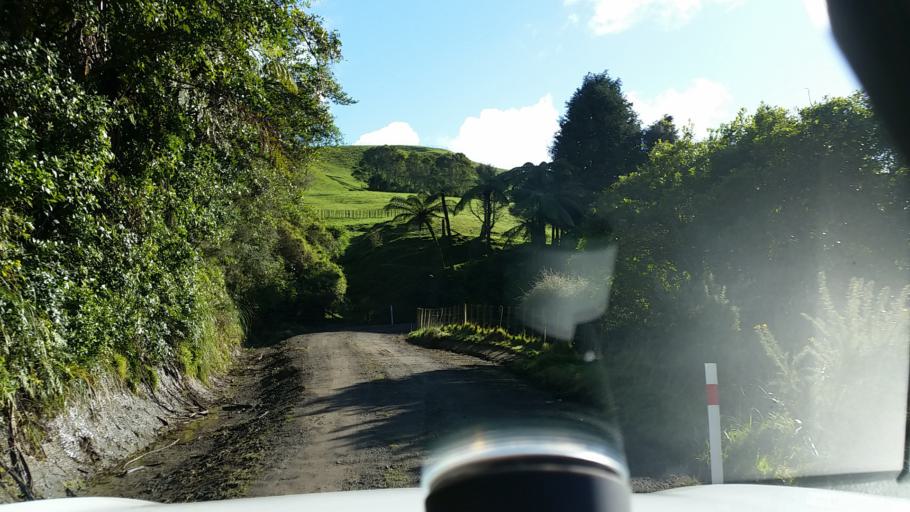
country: NZ
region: Taranaki
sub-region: South Taranaki District
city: Eltham
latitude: -39.4590
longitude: 174.3694
